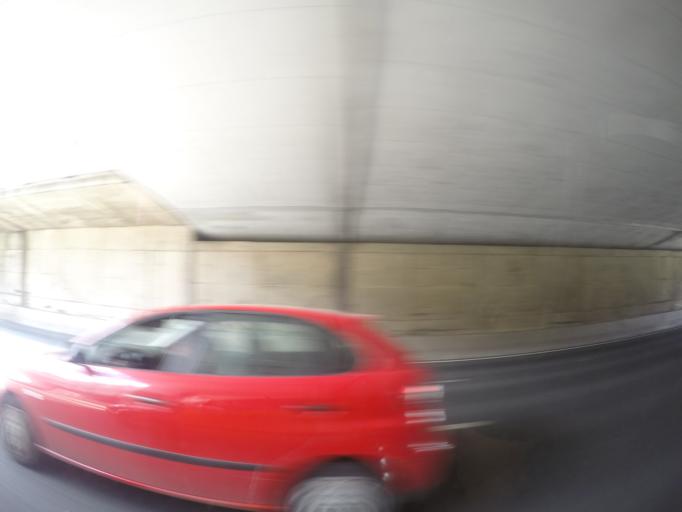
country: ES
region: Catalonia
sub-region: Provincia de Barcelona
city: Sant Marti
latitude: 41.4171
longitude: 2.2051
